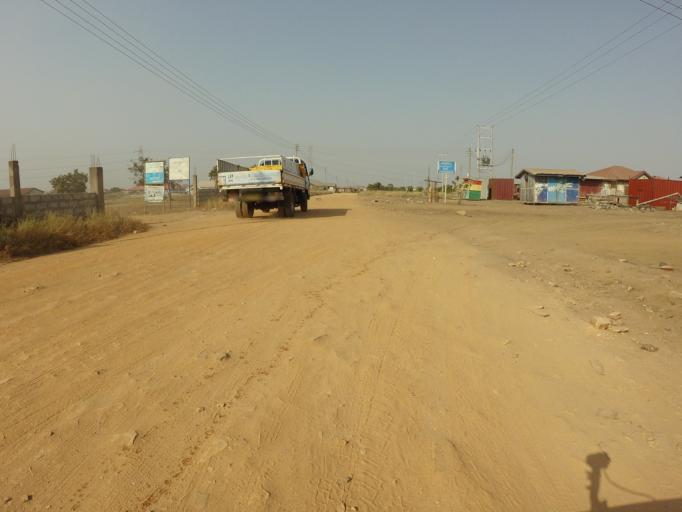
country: GH
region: Greater Accra
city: Tema
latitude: 5.7078
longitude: 0.0577
